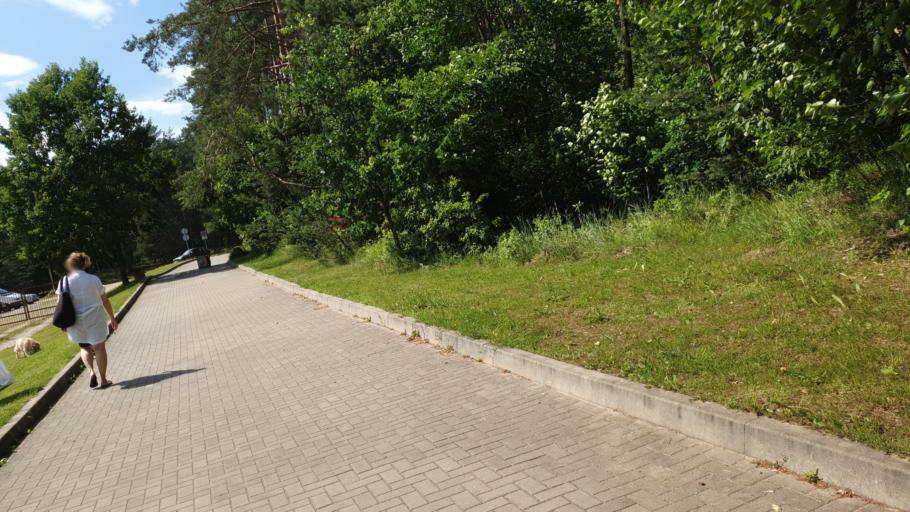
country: LT
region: Vilnius County
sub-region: Vilnius
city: Fabijoniskes
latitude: 54.7928
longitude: 25.3036
